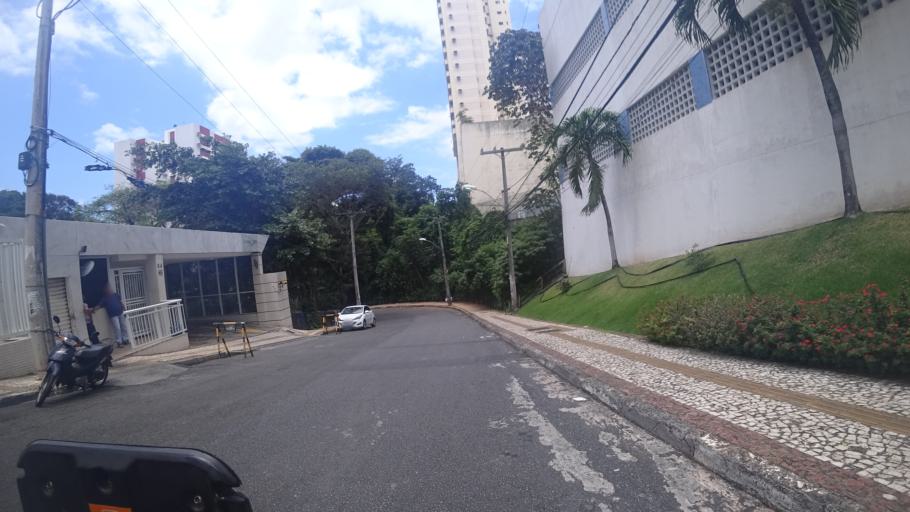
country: BR
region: Bahia
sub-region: Salvador
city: Salvador
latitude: -12.9927
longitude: -38.4739
